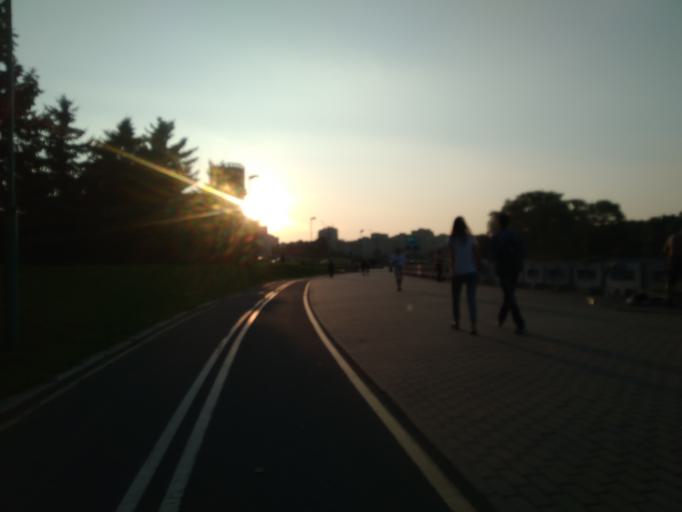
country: BY
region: Minsk
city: Minsk
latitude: 53.9119
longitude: 27.5486
